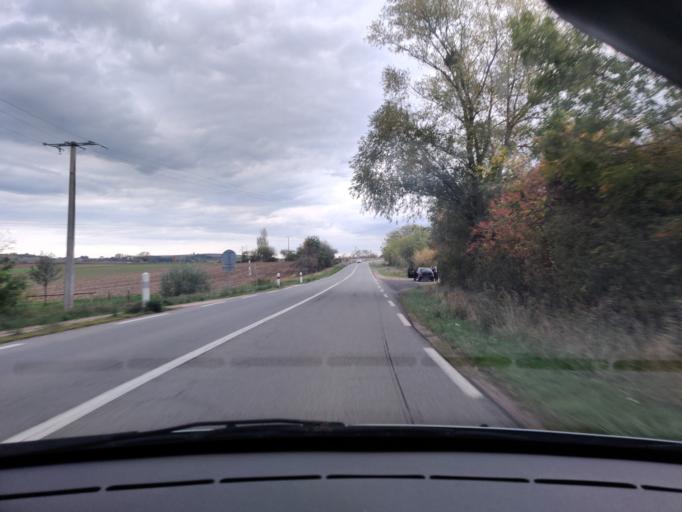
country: FR
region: Auvergne
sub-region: Departement du Puy-de-Dome
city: Saint-Bonnet-pres-Riom
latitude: 45.9497
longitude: 3.1074
